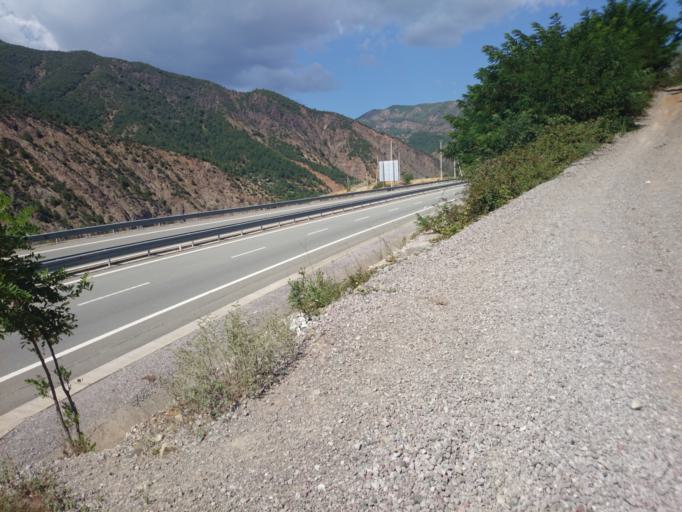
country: AL
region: Lezhe
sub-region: Rrethi i Lezhes
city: Blinisht
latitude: 41.8666
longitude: 20.0205
